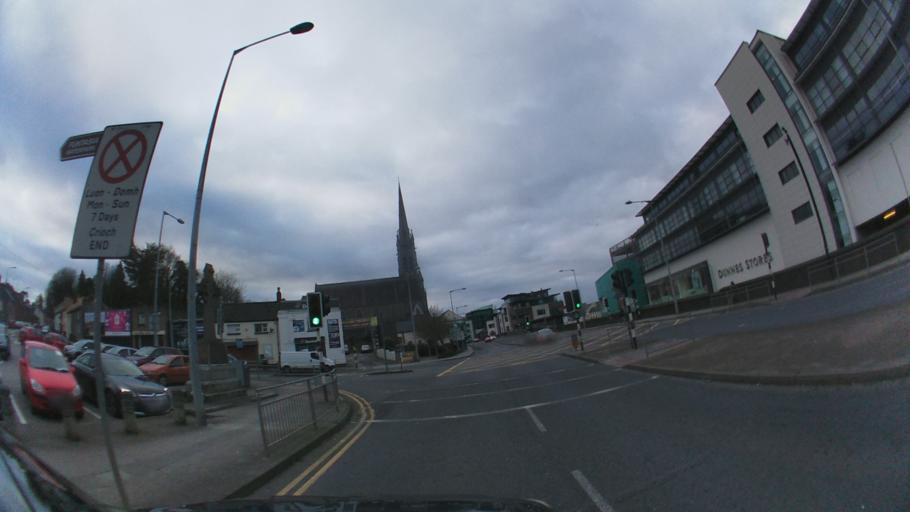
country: IE
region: Leinster
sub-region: Lu
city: Drogheda
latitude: 53.7129
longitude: -6.3394
